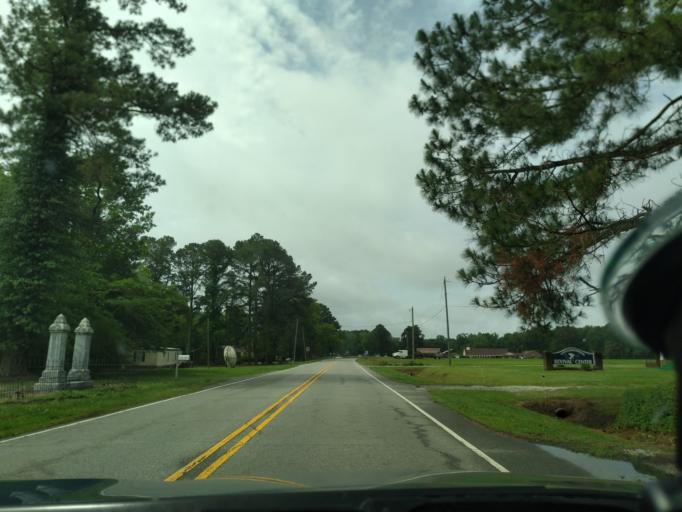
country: US
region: North Carolina
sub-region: Washington County
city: Plymouth
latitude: 35.8868
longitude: -76.6079
